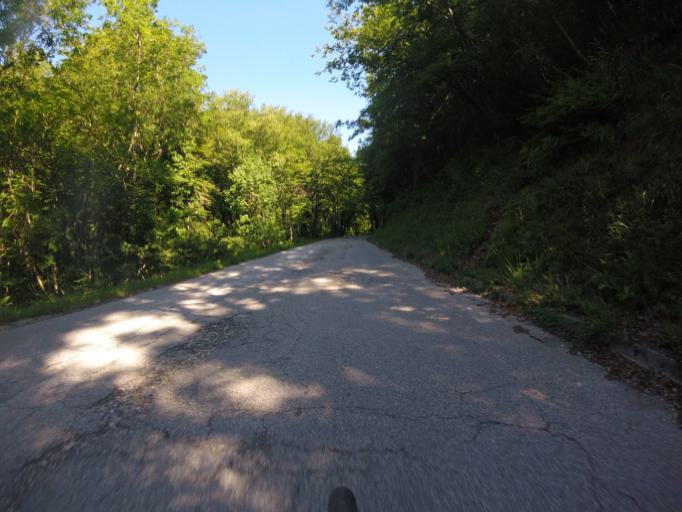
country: SI
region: Brezice
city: Brezice
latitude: 45.8378
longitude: 15.6001
